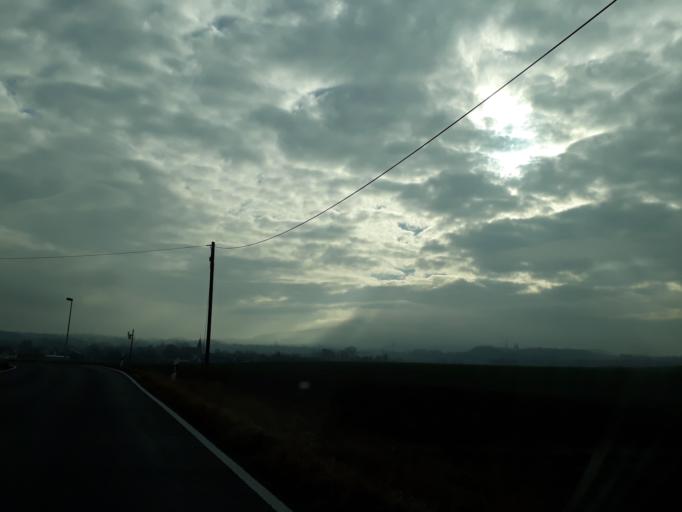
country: DE
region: Saxony
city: Niedercunnersdorf
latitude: 51.0631
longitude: 14.6496
